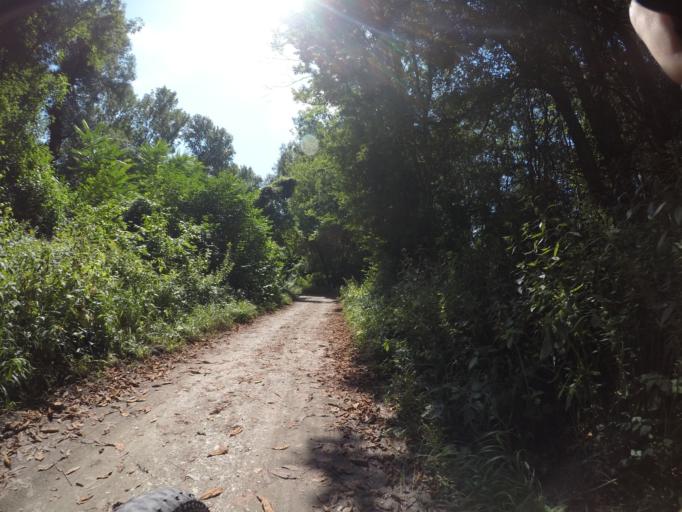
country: AT
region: Lower Austria
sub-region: Politischer Bezirk Wien-Umgebung
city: Schwechat
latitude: 48.1886
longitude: 16.4899
